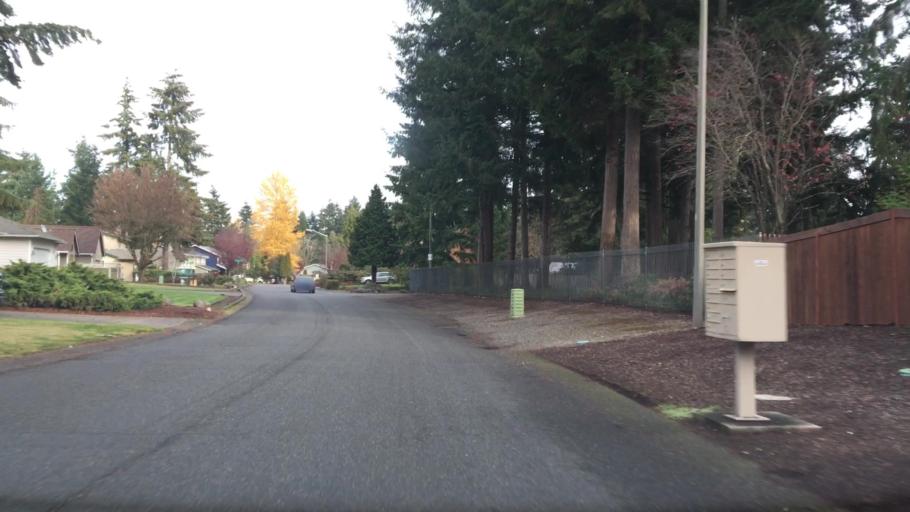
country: US
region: Washington
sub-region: Pierce County
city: South Hill
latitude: 47.1087
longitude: -122.3061
